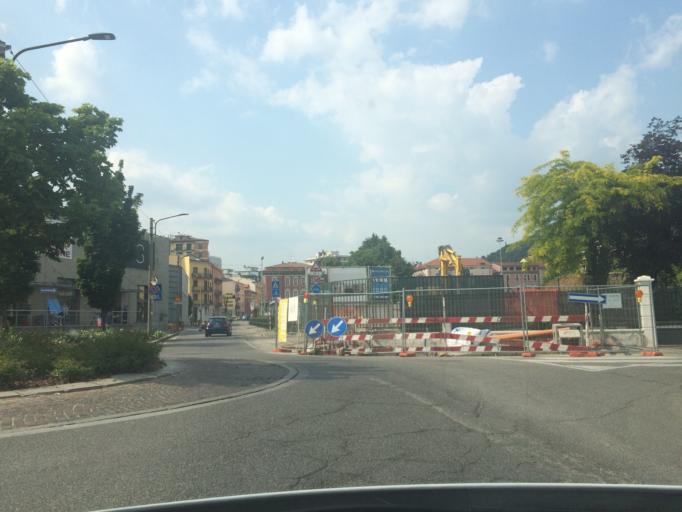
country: IT
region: Lombardy
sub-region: Provincia di Brescia
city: Brescia
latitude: 45.5325
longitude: 10.2359
